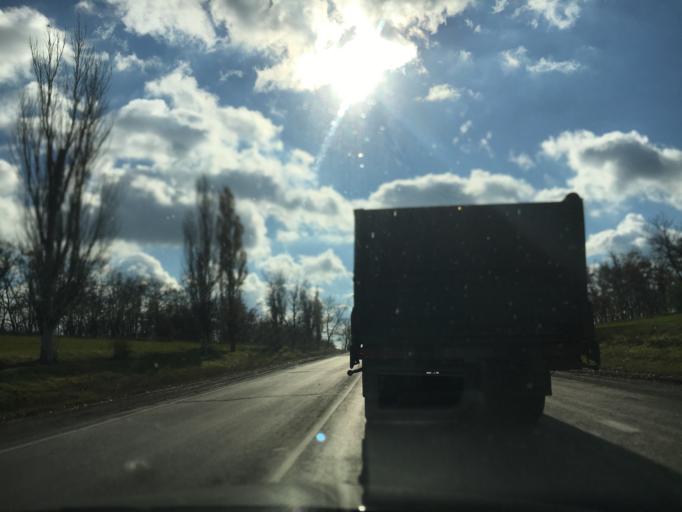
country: RU
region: Rostov
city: Matveyev Kurgan
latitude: 47.5429
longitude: 38.8912
